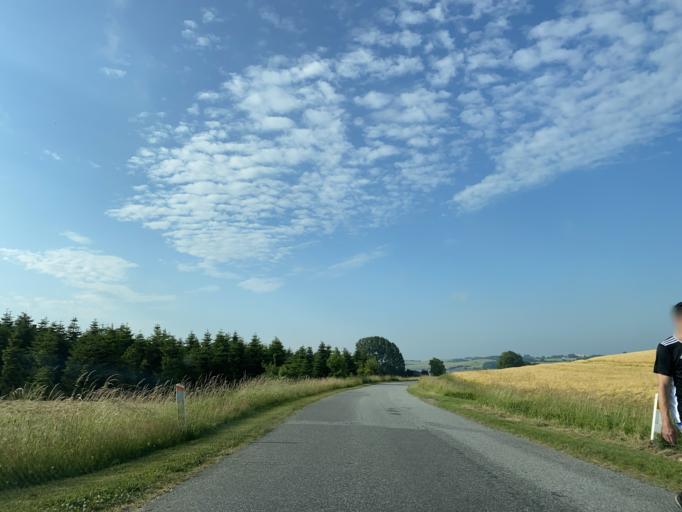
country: DK
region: South Denmark
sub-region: Haderslev Kommune
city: Haderslev
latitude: 55.1803
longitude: 9.4816
